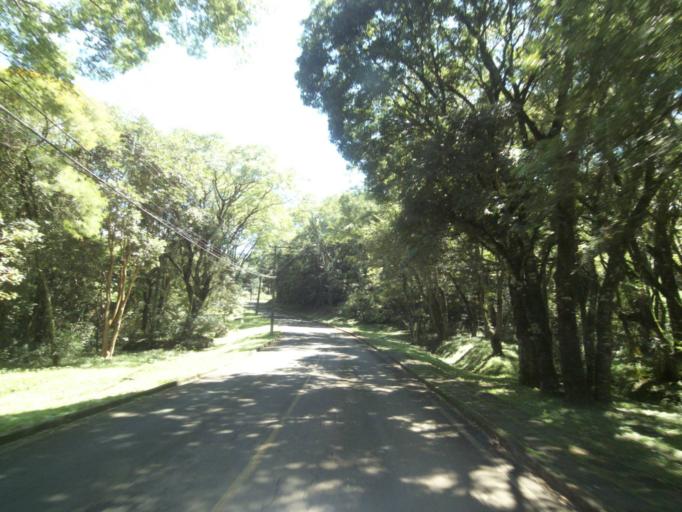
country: BR
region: Parana
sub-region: Chopinzinho
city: Chopinzinho
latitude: -25.7960
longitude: -52.0950
